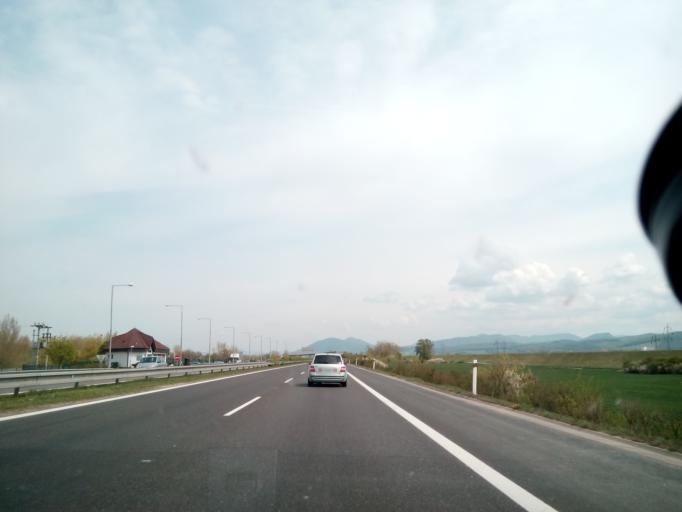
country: SK
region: Nitriansky
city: Dubnica nad Vahom
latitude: 48.9682
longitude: 18.1510
